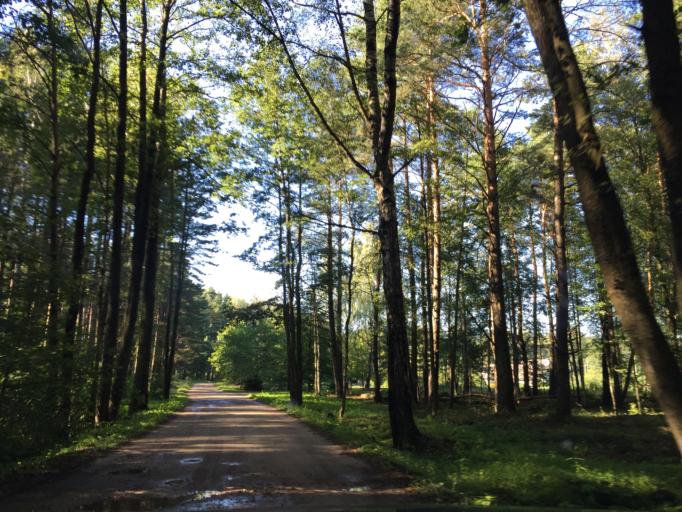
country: LV
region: Riga
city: Jaunciems
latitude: 57.0668
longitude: 24.1379
